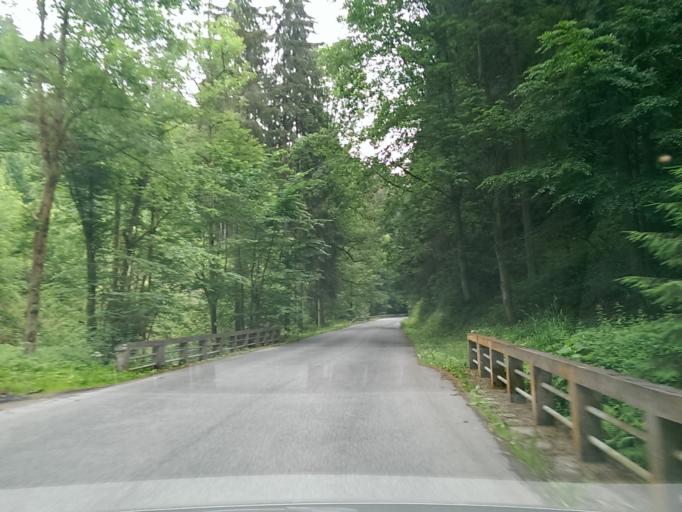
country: CZ
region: Liberecky
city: Semily
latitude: 50.6303
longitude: 15.3344
